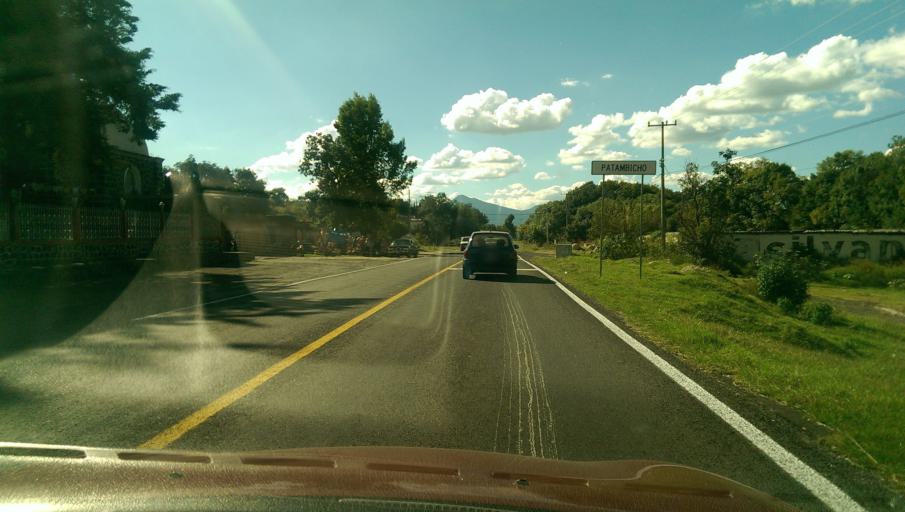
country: MX
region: Michoacan
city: Quiroga
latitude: 19.6398
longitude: -101.5413
